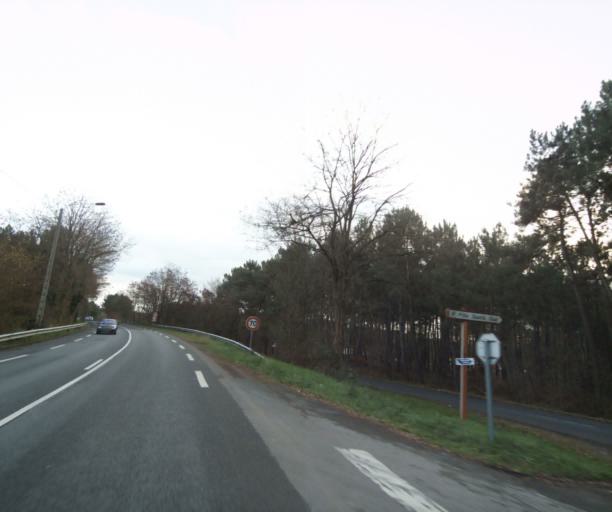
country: FR
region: Pays de la Loire
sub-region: Departement de la Sarthe
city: Ruaudin
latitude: 47.9699
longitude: 0.2335
